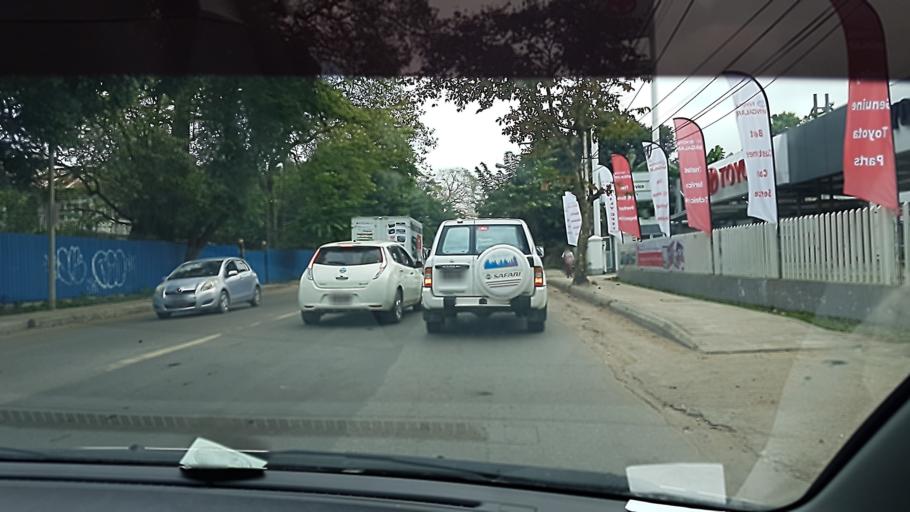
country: MM
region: Yangon
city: Yangon
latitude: 16.7905
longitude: 96.1321
